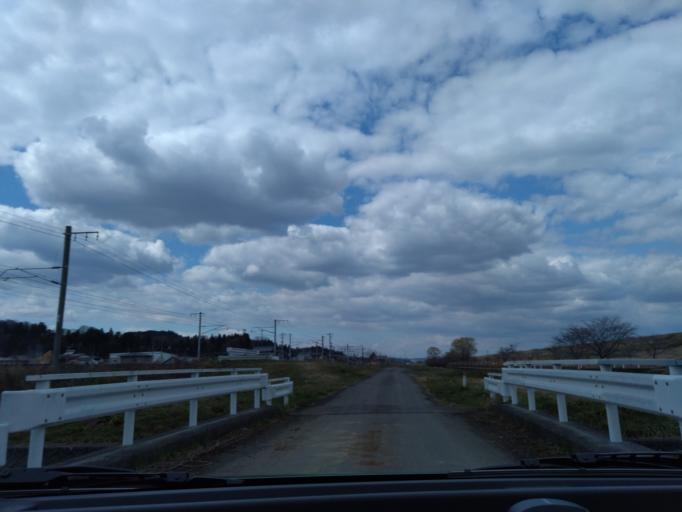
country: JP
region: Iwate
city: Ichinoseki
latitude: 38.9467
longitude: 141.1341
